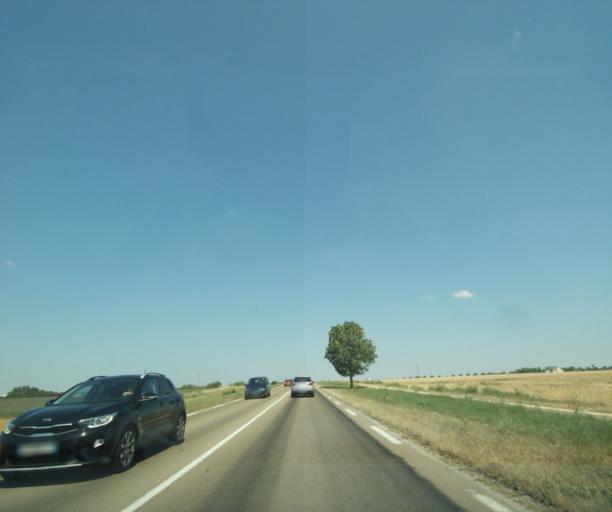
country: FR
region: Champagne-Ardenne
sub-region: Departement de la Marne
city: Sarry
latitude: 48.9311
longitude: 4.4066
